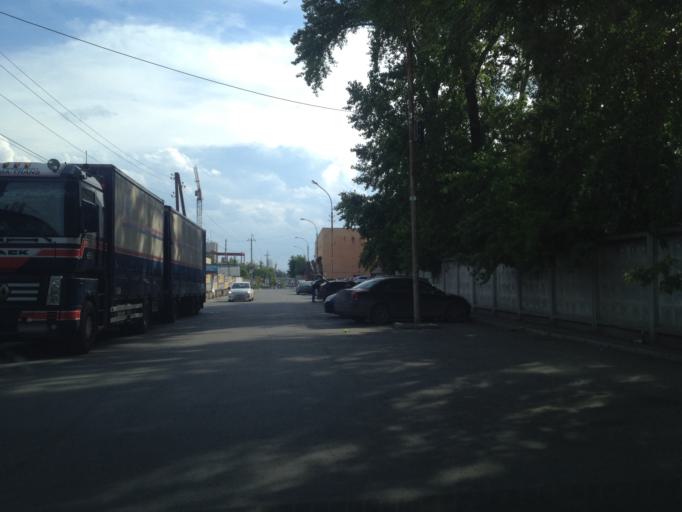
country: RU
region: Sverdlovsk
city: Yekaterinburg
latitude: 56.8242
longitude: 60.5589
